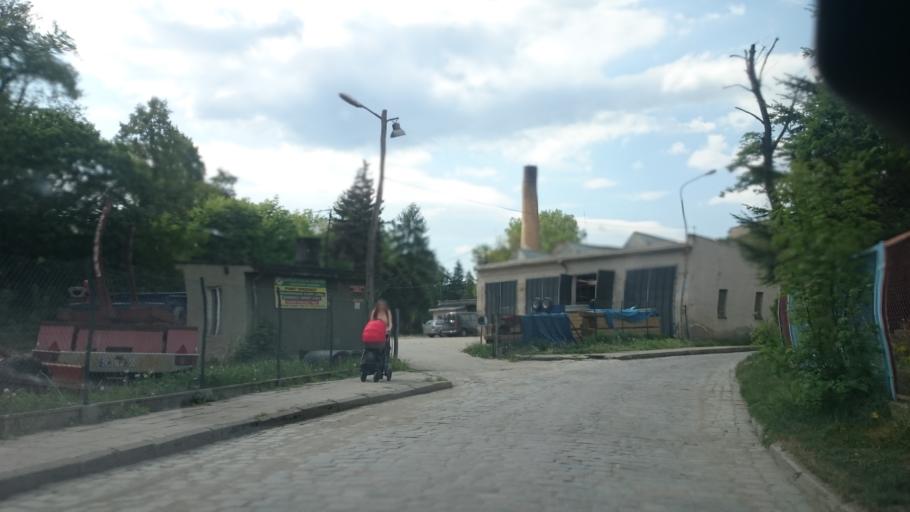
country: PL
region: Lower Silesian Voivodeship
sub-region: Powiat klodzki
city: Bystrzyca Klodzka
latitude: 50.2968
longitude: 16.6478
